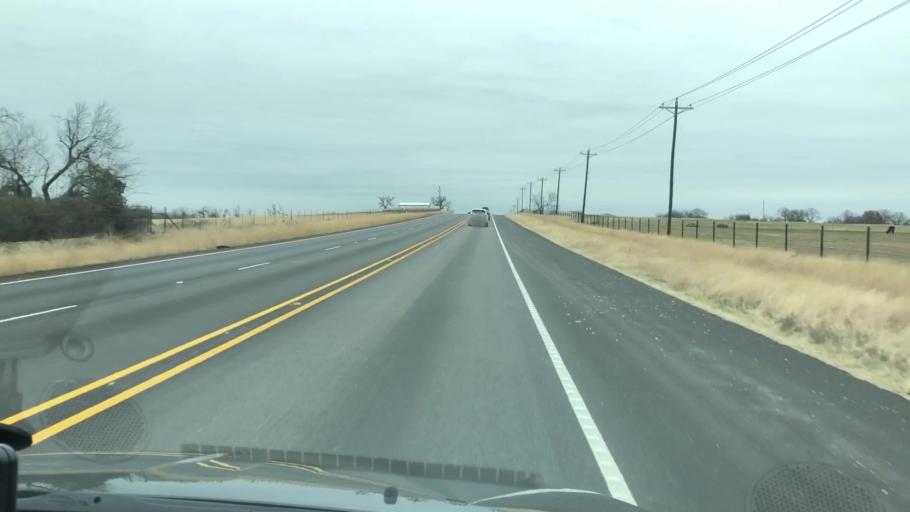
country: US
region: Texas
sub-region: Erath County
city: Stephenville
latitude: 32.2919
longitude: -98.1904
